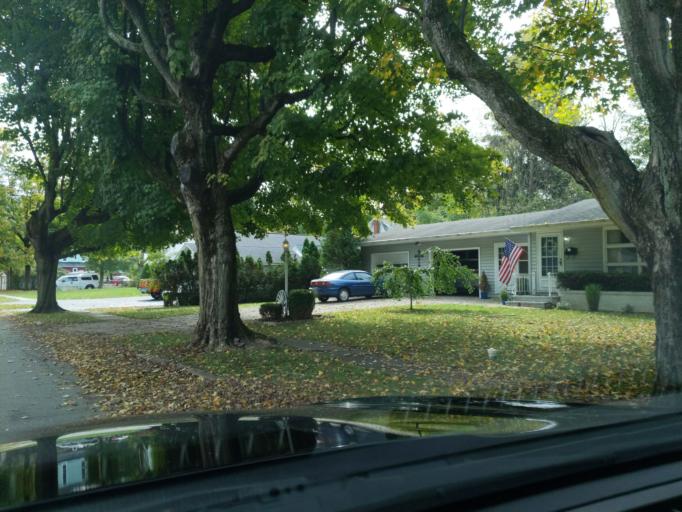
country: US
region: Pennsylvania
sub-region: Blair County
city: Hollidaysburg
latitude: 40.4299
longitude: -78.4055
